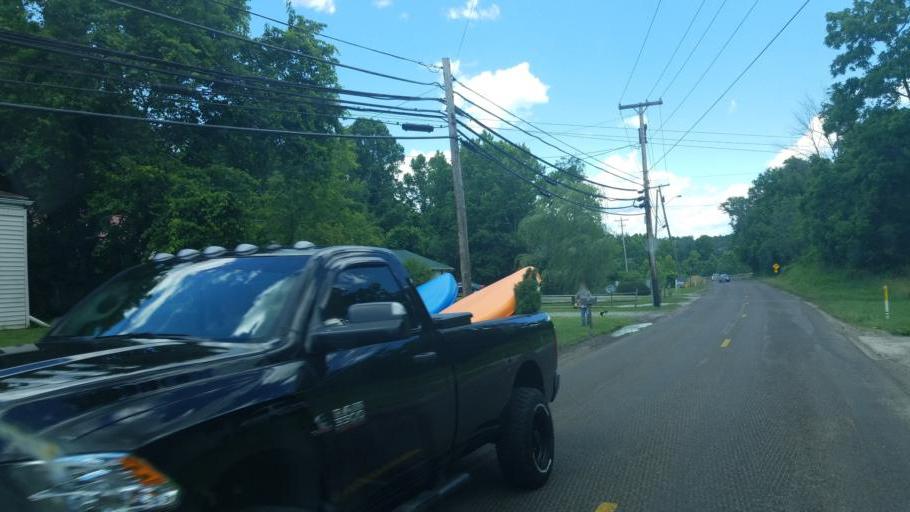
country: US
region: Ohio
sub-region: Gallia County
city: Gallipolis
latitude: 38.8038
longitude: -82.2225
